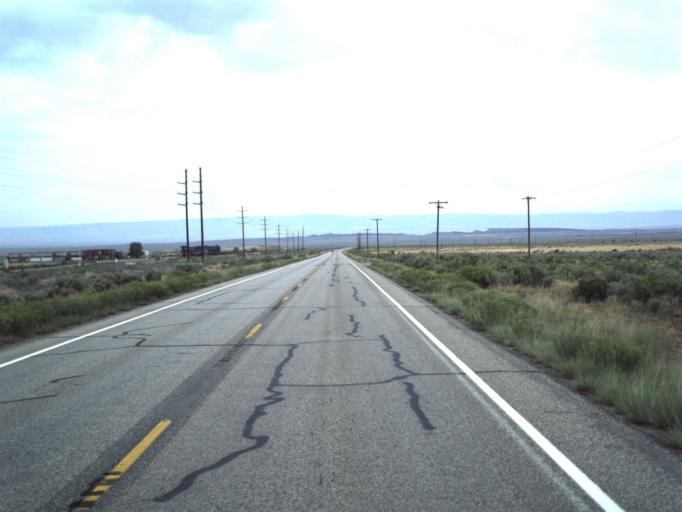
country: US
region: Utah
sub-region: Carbon County
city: East Carbon City
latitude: 39.5356
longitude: -110.4781
